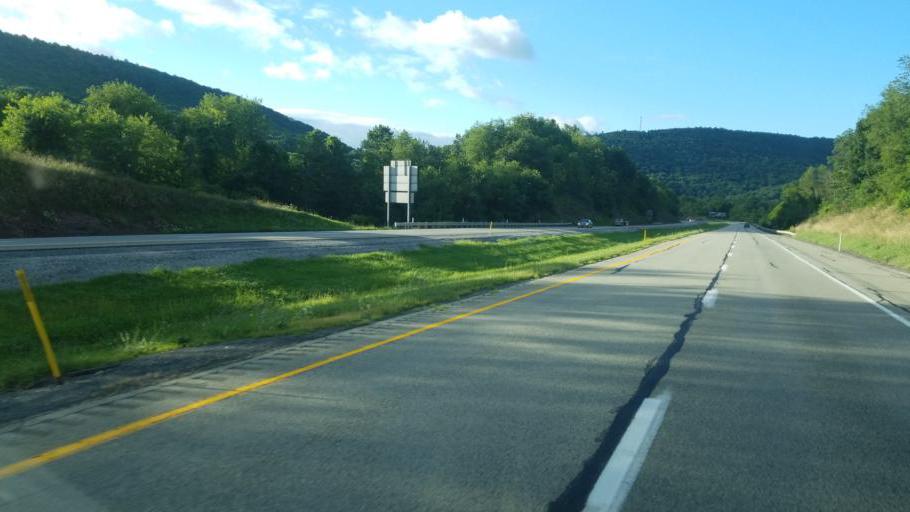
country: US
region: Pennsylvania
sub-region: Bedford County
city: Earlston
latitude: 39.9632
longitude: -78.2475
